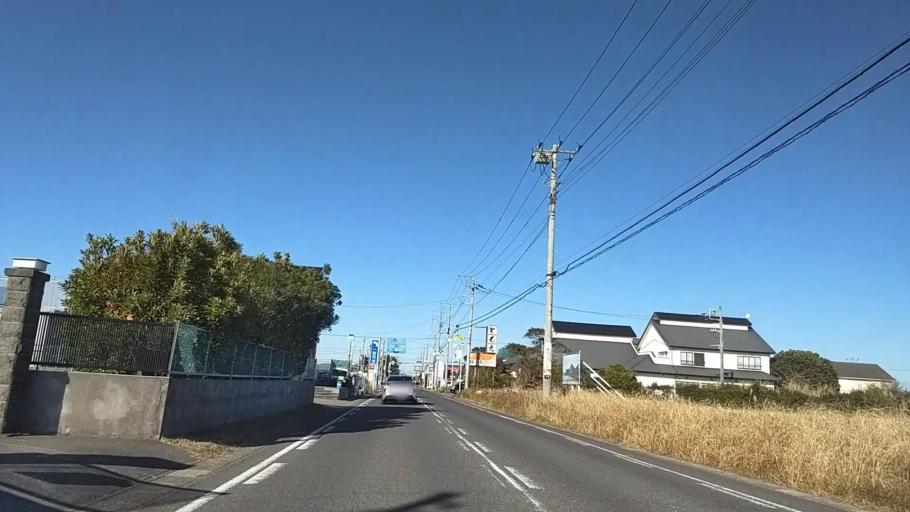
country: JP
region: Chiba
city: Mobara
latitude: 35.3718
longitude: 140.3876
